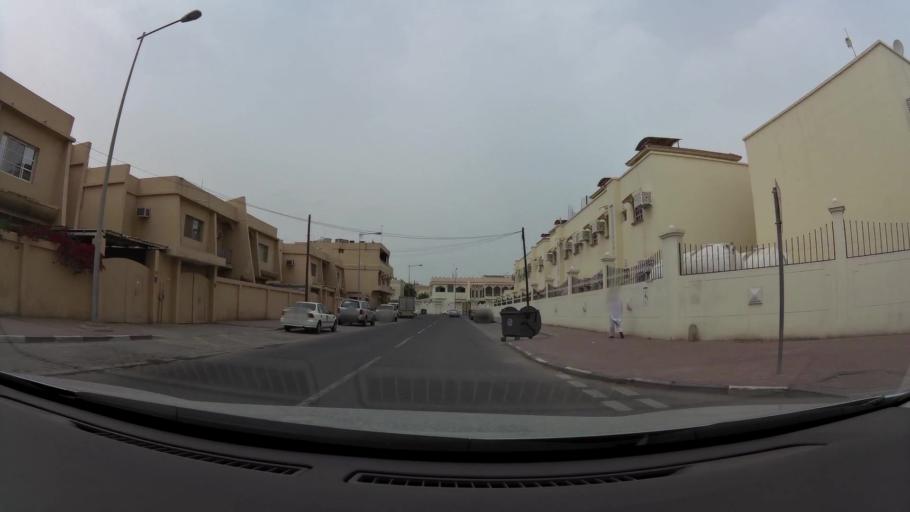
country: QA
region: Baladiyat ad Dawhah
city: Doha
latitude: 25.2479
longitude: 51.5625
